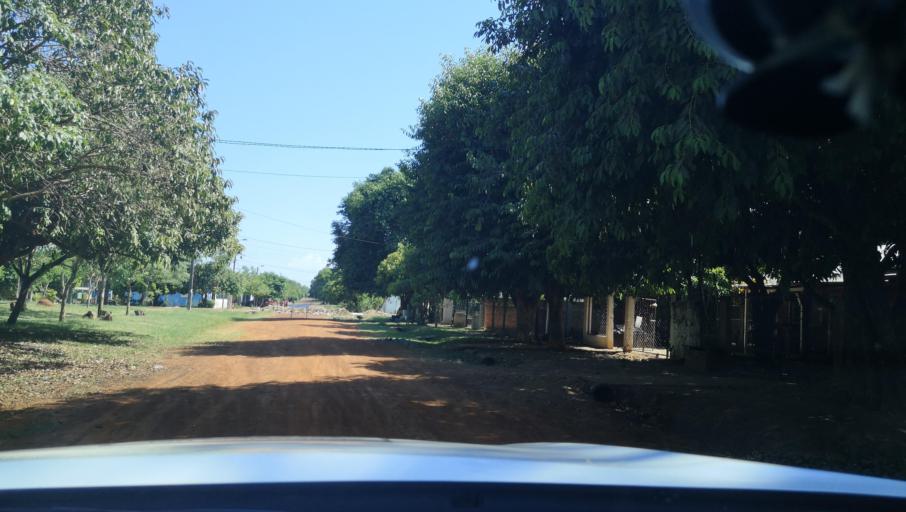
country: PY
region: Itapua
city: Carmen del Parana
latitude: -27.1679
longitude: -56.2311
